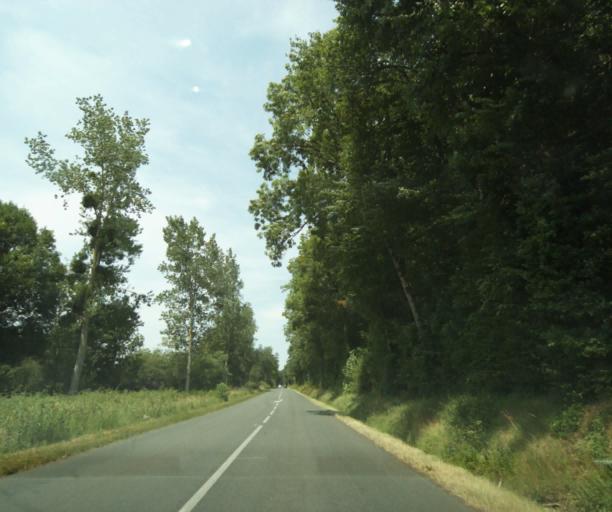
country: FR
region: Poitou-Charentes
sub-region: Departement de la Vienne
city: Lussac-les-Chateaux
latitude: 46.4246
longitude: 0.6893
